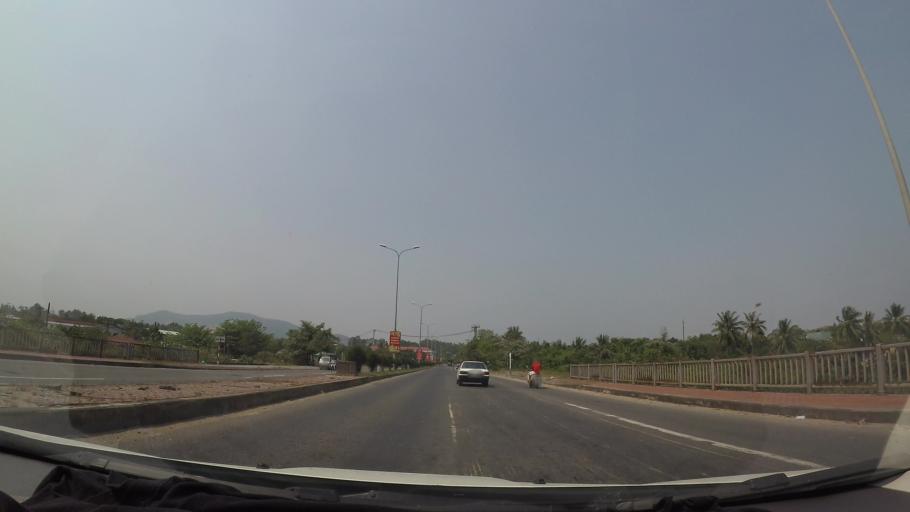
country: VN
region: Da Nang
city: Cam Le
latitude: 16.0004
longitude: 108.1907
